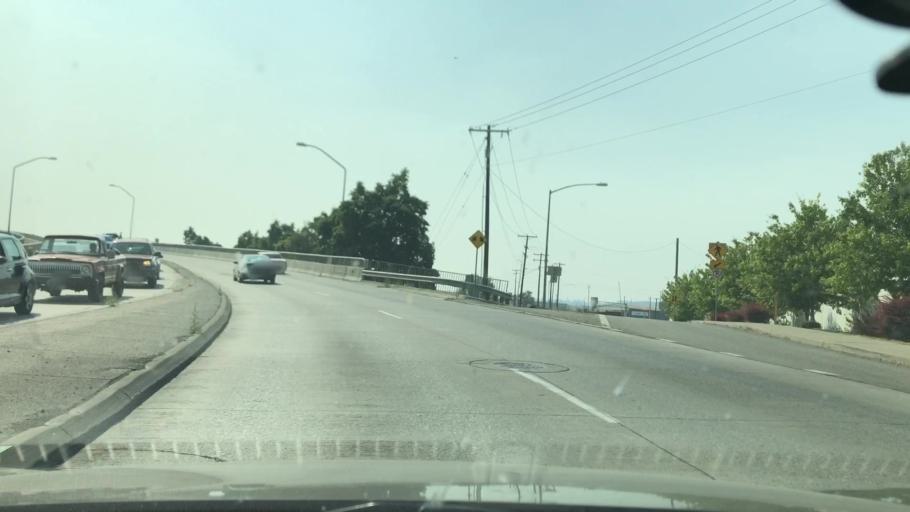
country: US
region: Washington
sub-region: Spokane County
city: Spokane
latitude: 47.6710
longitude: -117.3638
